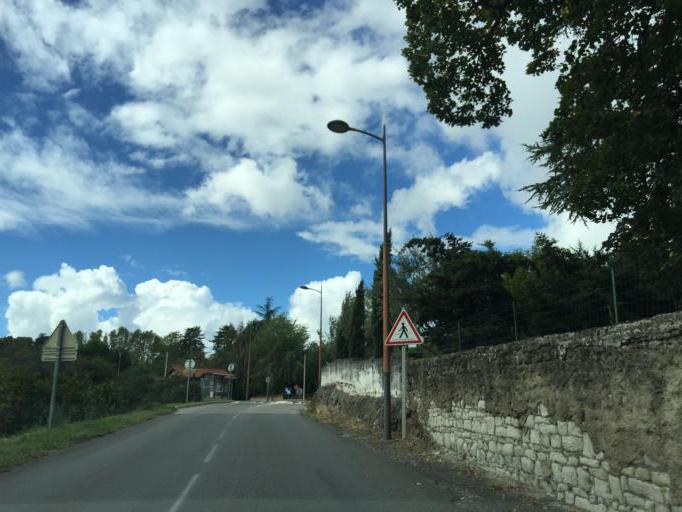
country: FR
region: Rhone-Alpes
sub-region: Departement de la Loire
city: Saint-Martin-la-Plaine
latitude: 45.5335
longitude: 4.5870
